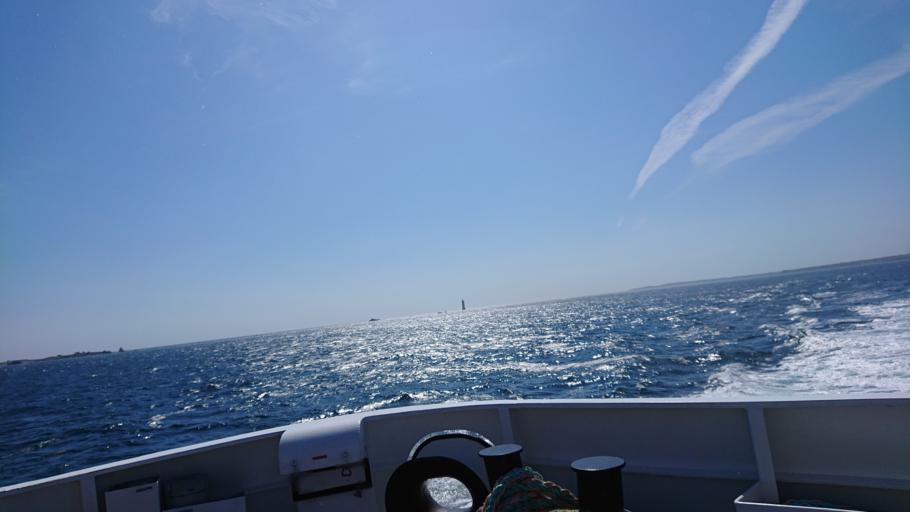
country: FR
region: Brittany
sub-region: Departement du Finistere
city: Lampaul-Plouarzel
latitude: 48.4456
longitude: -4.9955
